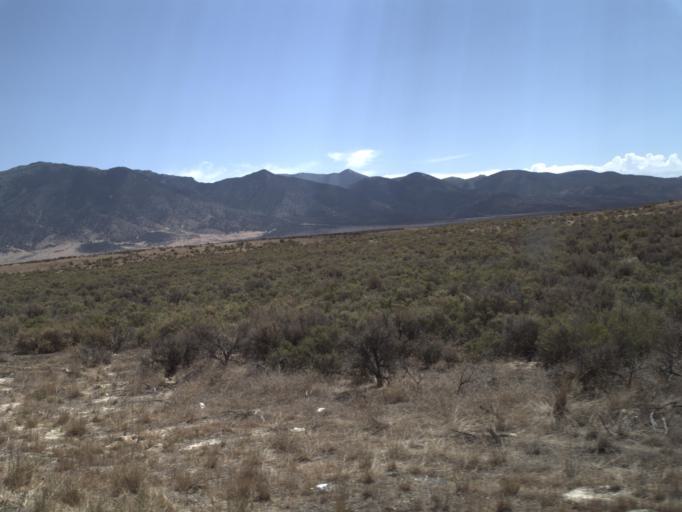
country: US
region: Utah
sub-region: Tooele County
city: Tooele
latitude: 40.3705
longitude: -112.4015
